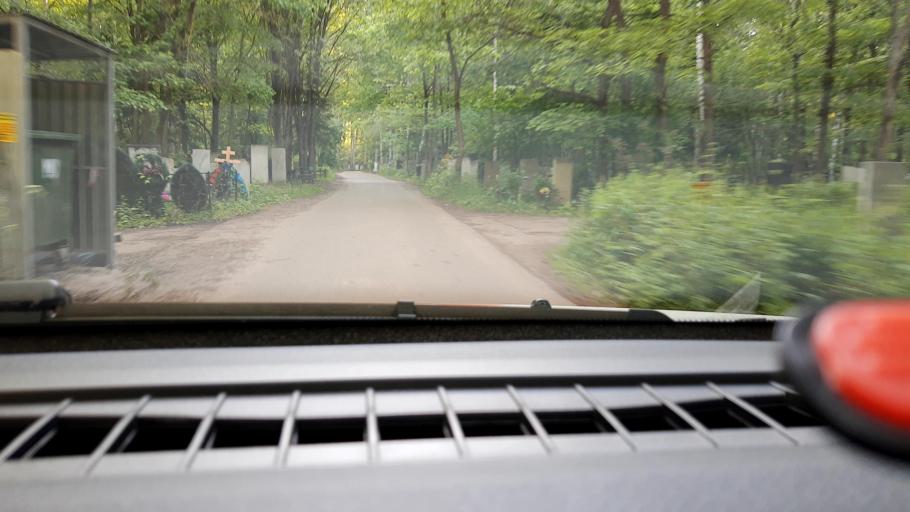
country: RU
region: Nizjnij Novgorod
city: Gorbatovka
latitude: 56.2322
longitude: 43.7712
